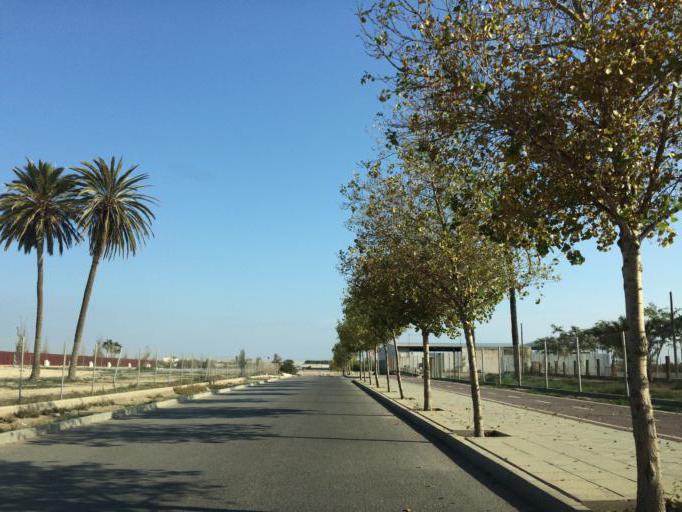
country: ES
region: Andalusia
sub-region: Provincia de Almeria
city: Almeria
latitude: 36.8323
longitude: -2.4309
